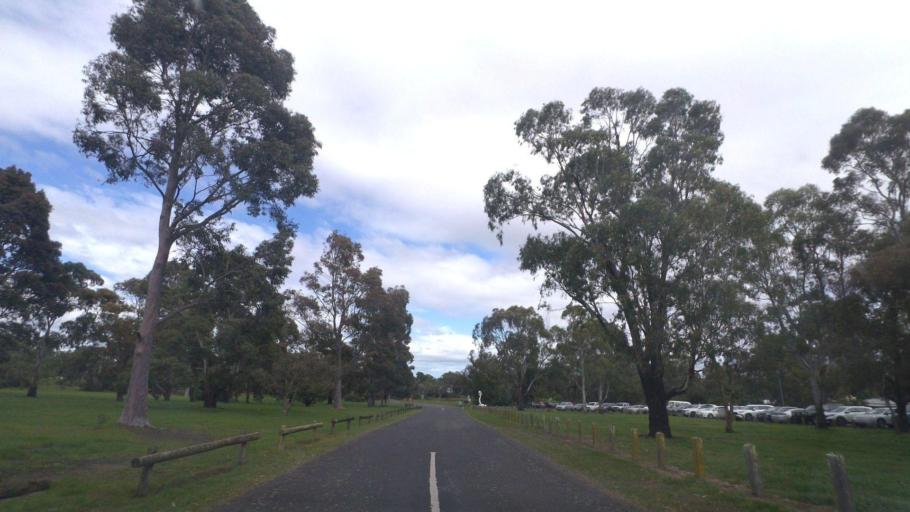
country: AU
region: Victoria
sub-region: Darebin
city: Kingsbury
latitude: -37.7064
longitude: 145.0457
